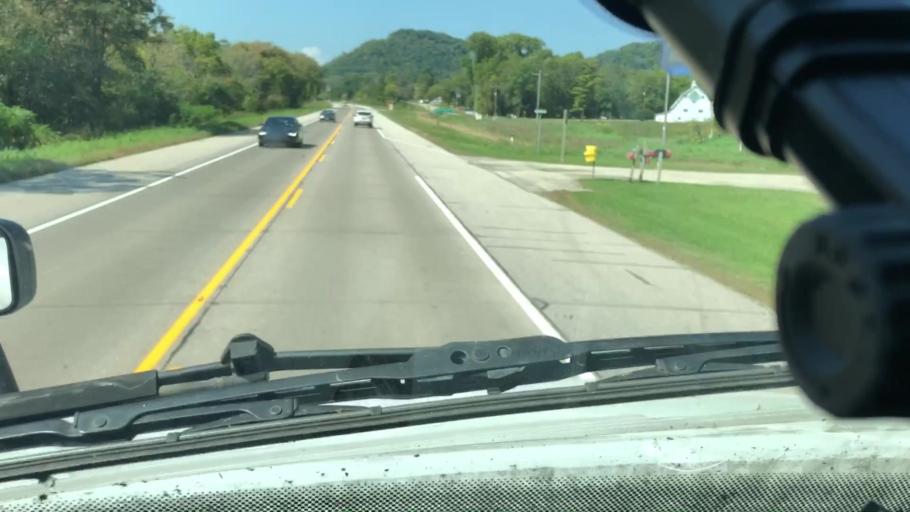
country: US
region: Minnesota
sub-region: Winona County
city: Winona
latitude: 44.0690
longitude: -91.5983
